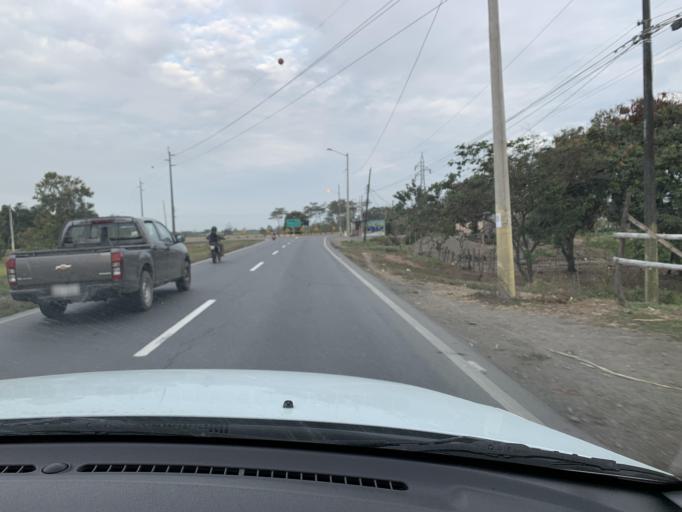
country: EC
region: Guayas
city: Yaguachi Nuevo
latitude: -2.2357
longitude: -79.6405
